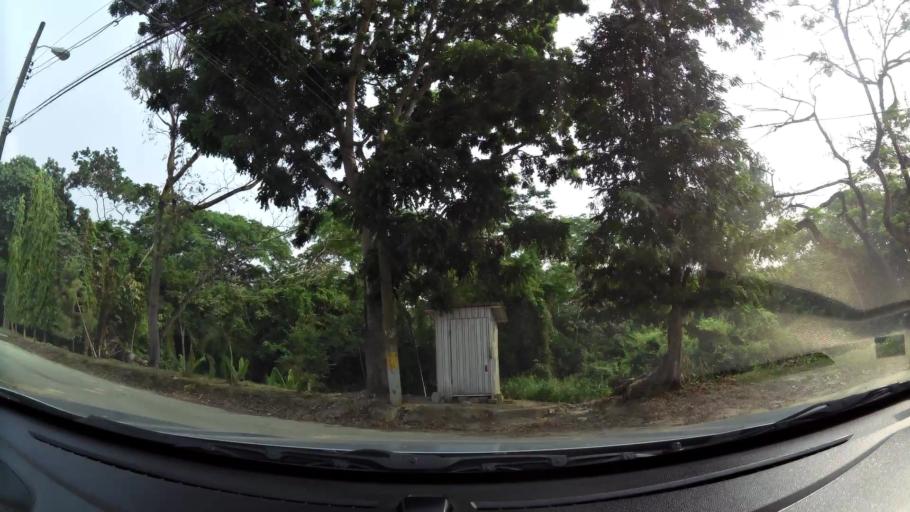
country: HN
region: Cortes
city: El Zapotal del Norte
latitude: 15.5196
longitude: -88.0451
